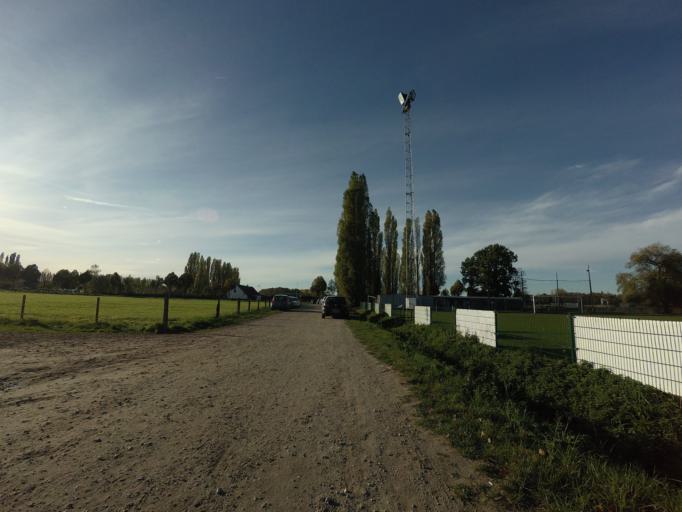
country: BE
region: Flanders
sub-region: Provincie Antwerpen
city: Brasschaat
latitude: 51.2632
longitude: 4.4485
